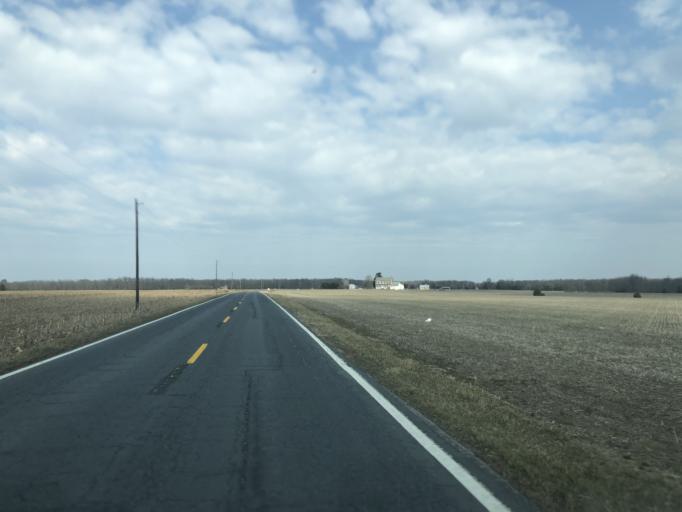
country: US
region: Maryland
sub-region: Caroline County
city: Ridgely
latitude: 39.0418
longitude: -75.9128
